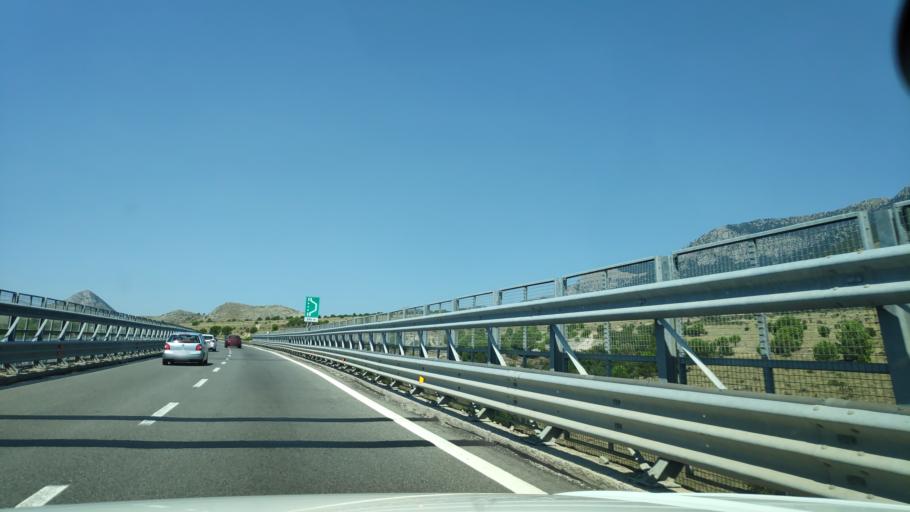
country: IT
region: Calabria
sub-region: Provincia di Cosenza
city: Frascineto
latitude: 39.8466
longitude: 16.2353
